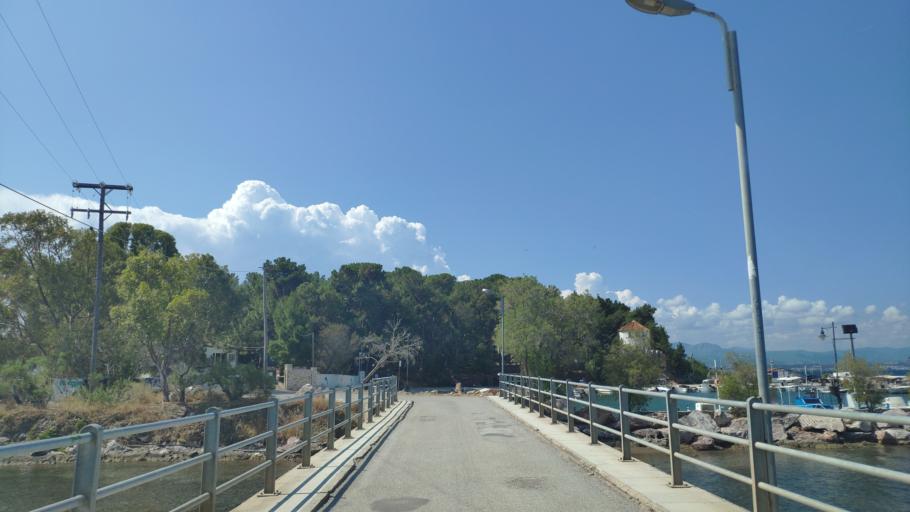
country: GR
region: Central Greece
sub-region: Nomos Evvoias
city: Eretria
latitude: 38.3865
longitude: 23.8009
